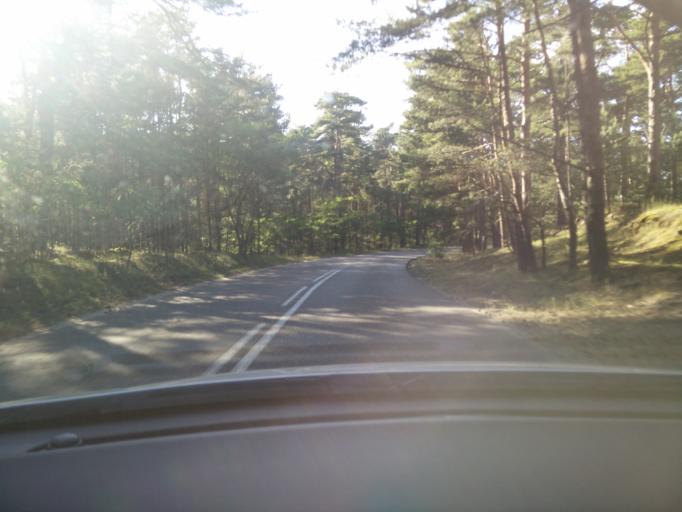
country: PL
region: Pomeranian Voivodeship
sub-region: Powiat pucki
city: Hel
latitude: 54.6588
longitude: 18.7510
